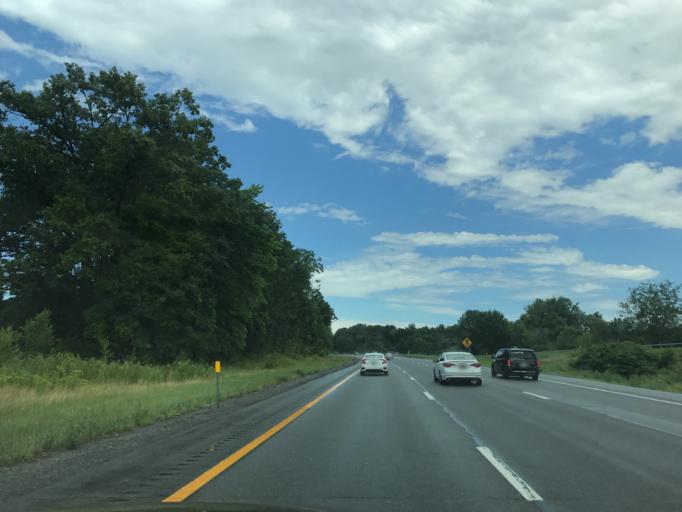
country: US
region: New York
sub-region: Albany County
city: Cohoes
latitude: 42.8195
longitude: -73.7671
